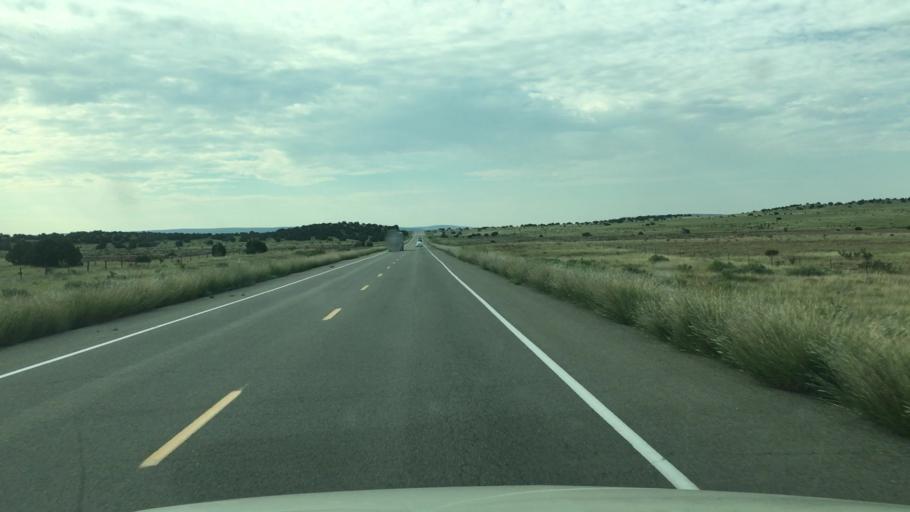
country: US
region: New Mexico
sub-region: Santa Fe County
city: Eldorado at Santa Fe
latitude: 35.4397
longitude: -105.8843
